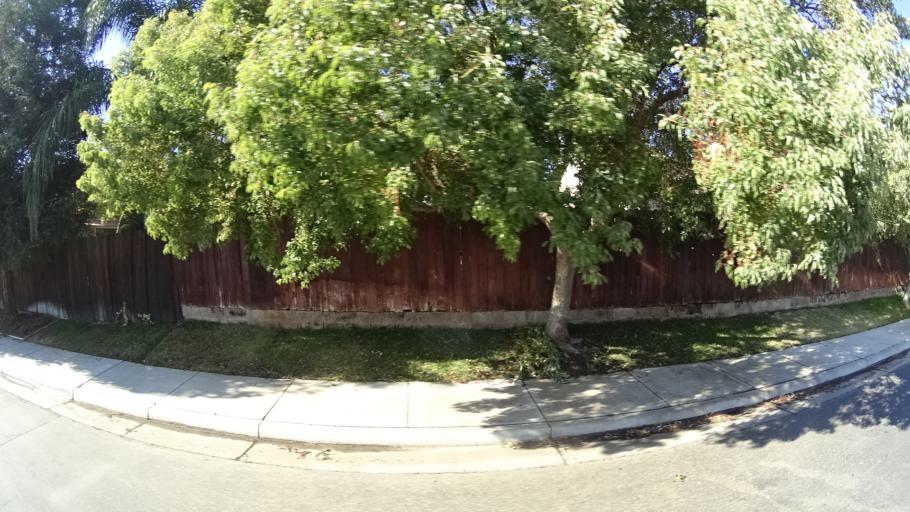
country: US
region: California
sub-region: Kern County
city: Rosedale
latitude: 35.3643
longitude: -119.1331
